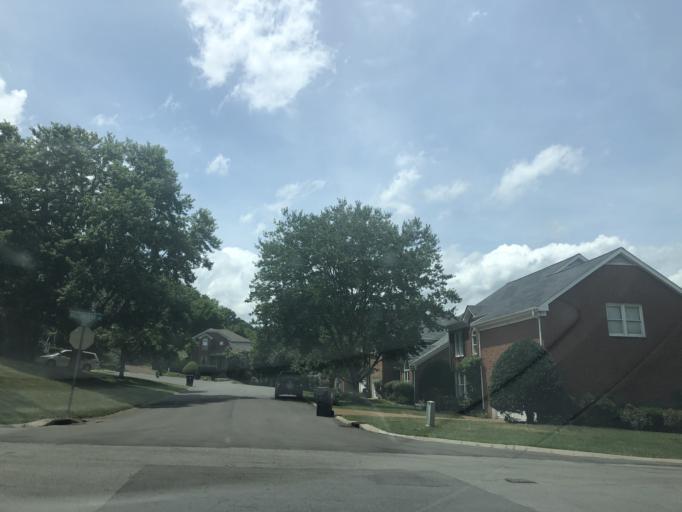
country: US
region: Tennessee
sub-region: Davidson County
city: Belle Meade
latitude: 36.0523
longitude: -86.9539
